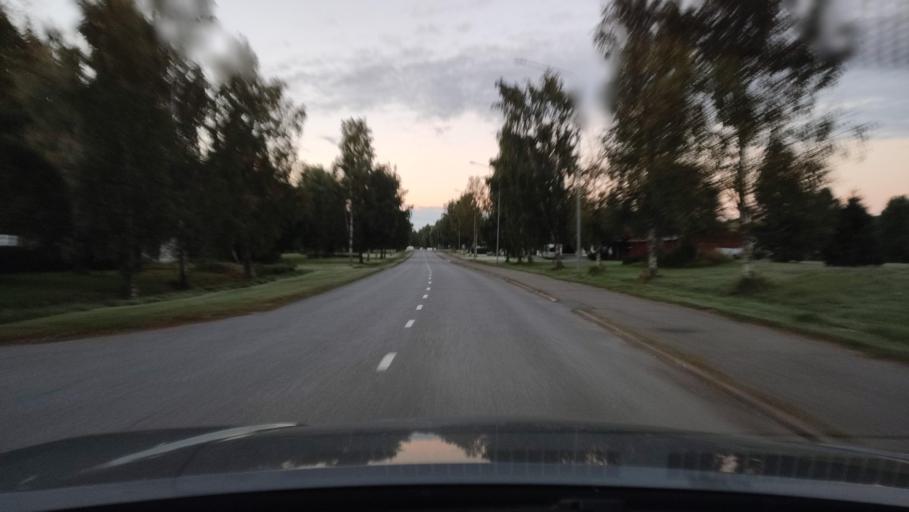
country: FI
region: Ostrobothnia
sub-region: Sydosterbotten
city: Kristinestad
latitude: 62.2795
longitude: 21.3636
